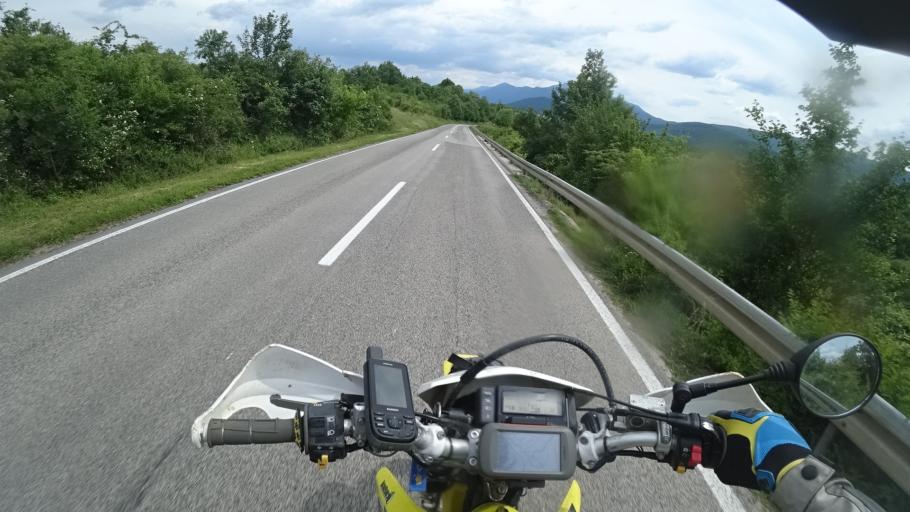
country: HR
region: Licko-Senjska
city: Jezerce
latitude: 44.9246
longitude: 15.7035
